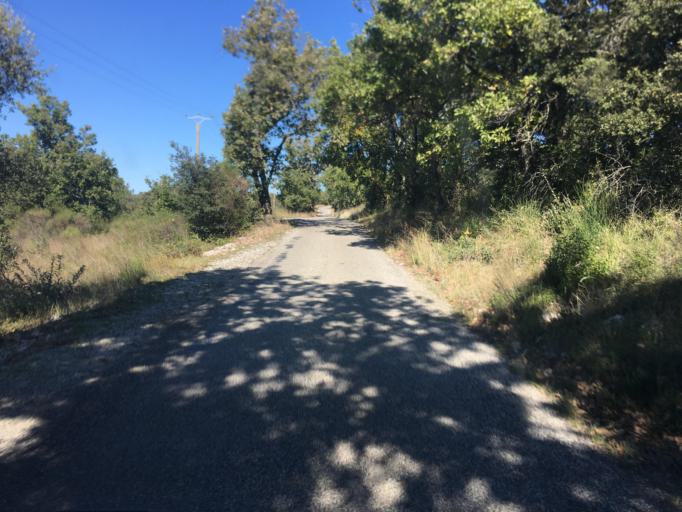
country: FR
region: Languedoc-Roussillon
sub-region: Departement du Gard
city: Montaren-et-Saint-Mediers
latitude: 44.1367
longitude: 4.3096
